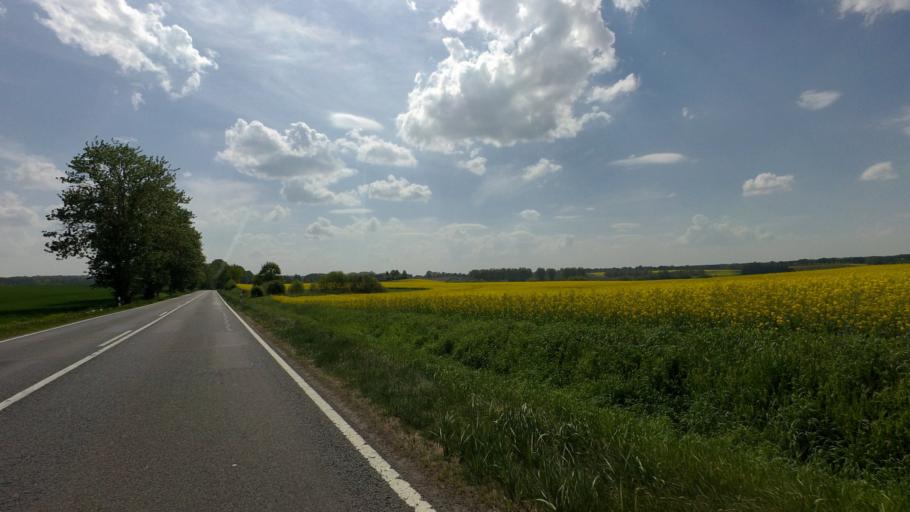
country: DE
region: Mecklenburg-Vorpommern
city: Mollenhagen
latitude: 53.5751
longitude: 12.8658
